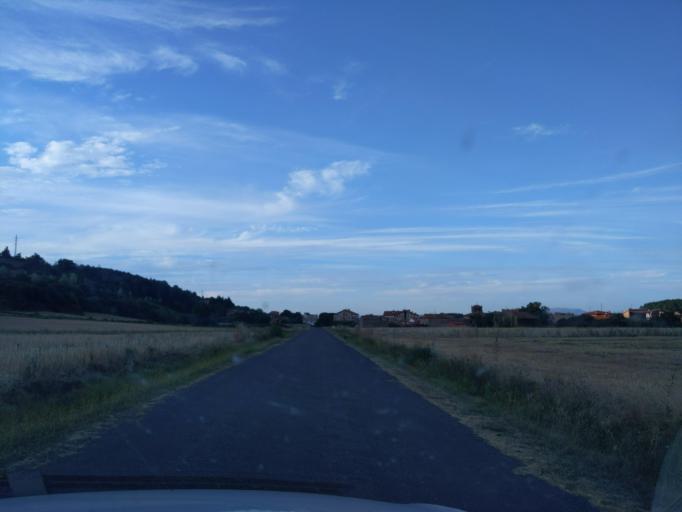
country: ES
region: La Rioja
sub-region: Provincia de La Rioja
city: Santurdejo
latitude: 42.3860
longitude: -2.9827
